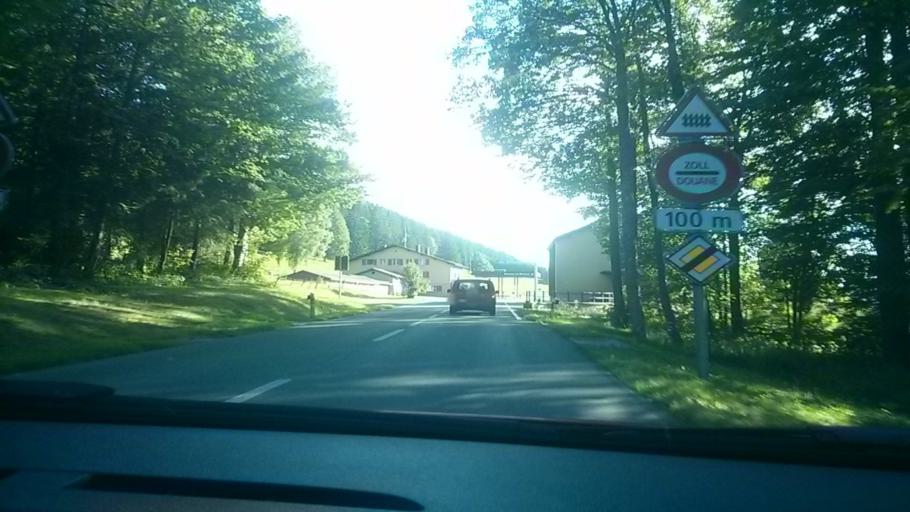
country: CH
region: Vaud
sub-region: Jura-Nord vaudois District
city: Le Chenit
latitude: 46.5495
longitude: 6.1601
